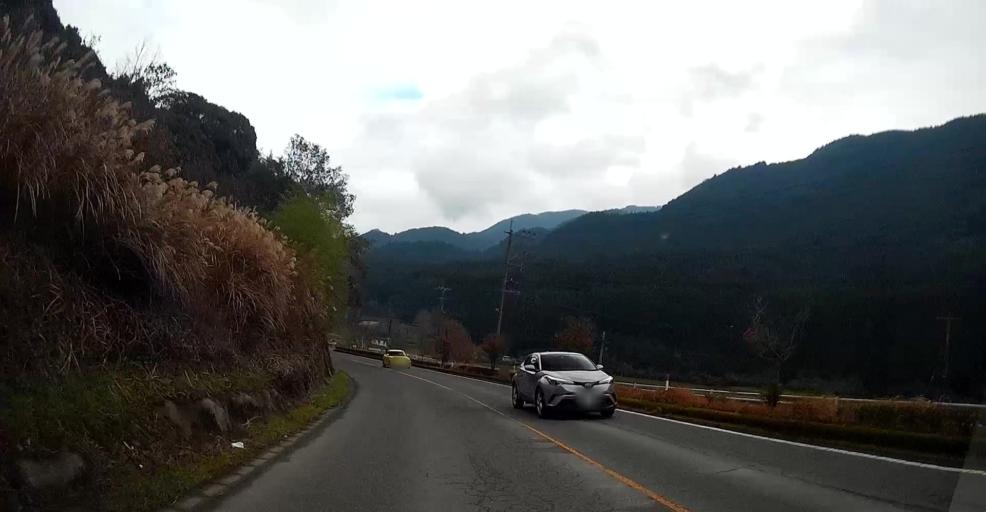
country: JP
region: Kumamoto
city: Matsubase
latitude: 32.6140
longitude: 130.8452
